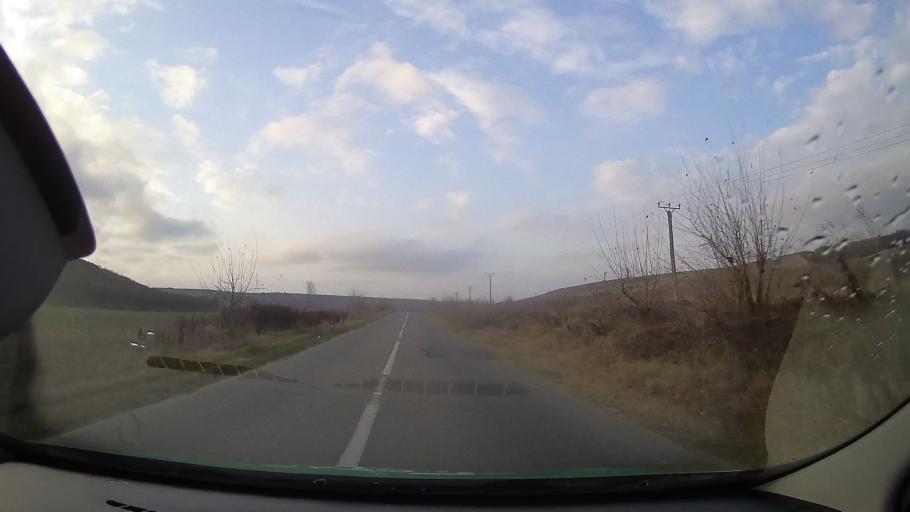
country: RO
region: Constanta
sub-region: Comuna Dobromir
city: Dobromir
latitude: 44.0331
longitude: 27.8555
